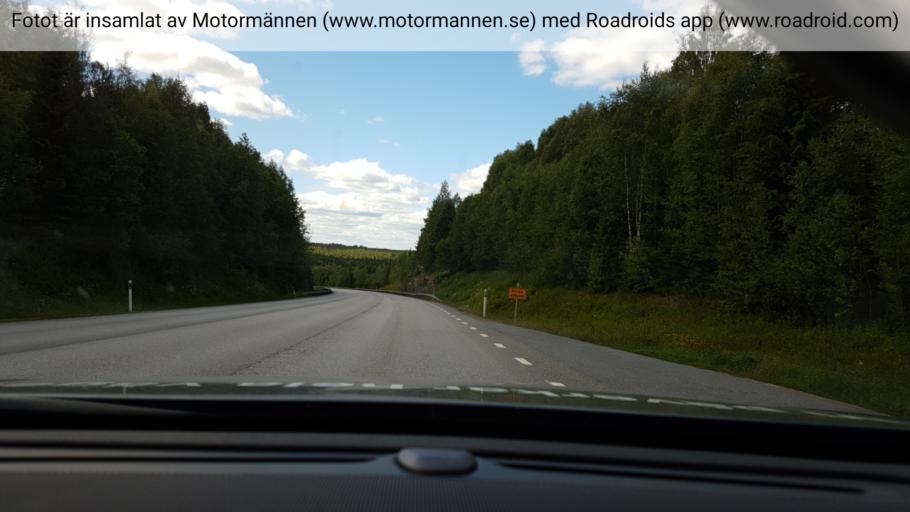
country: SE
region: Vaesterbotten
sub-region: Robertsfors Kommun
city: Robertsfors
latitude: 64.2952
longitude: 21.0967
